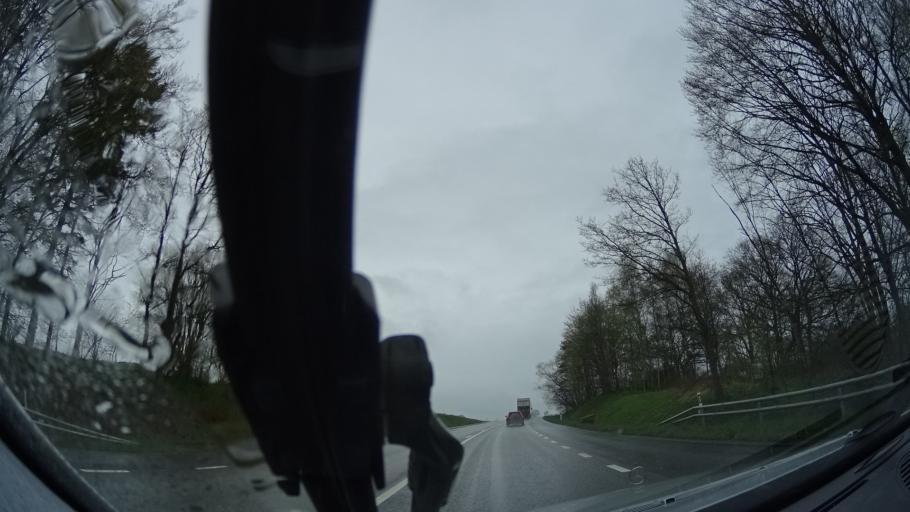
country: SE
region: Skane
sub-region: Hoors Kommun
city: Loberod
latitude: 55.8139
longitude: 13.4777
